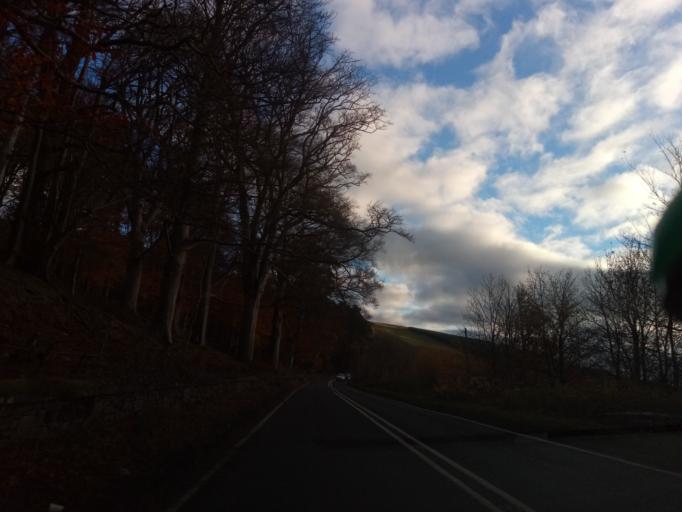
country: GB
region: Scotland
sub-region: The Scottish Borders
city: Galashiels
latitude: 55.6822
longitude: -2.8692
